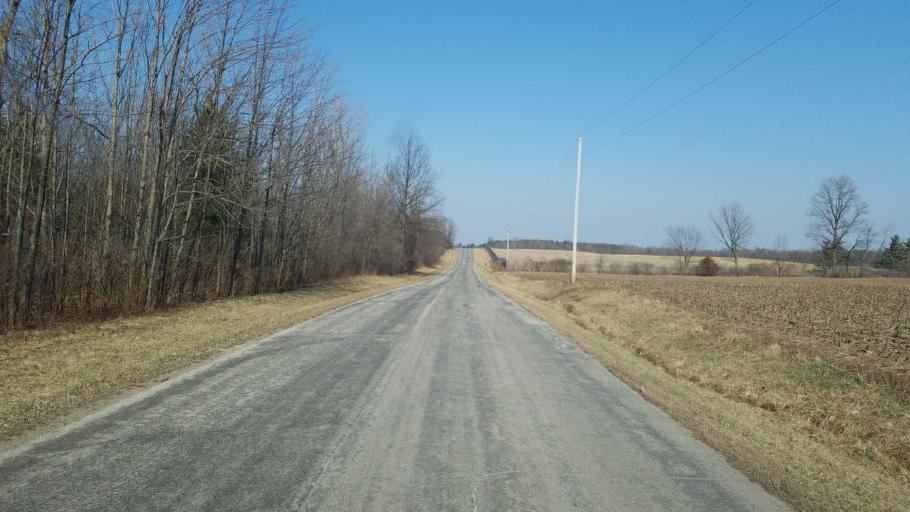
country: US
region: Ohio
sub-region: Richland County
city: Mansfield
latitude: 40.8294
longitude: -82.5327
